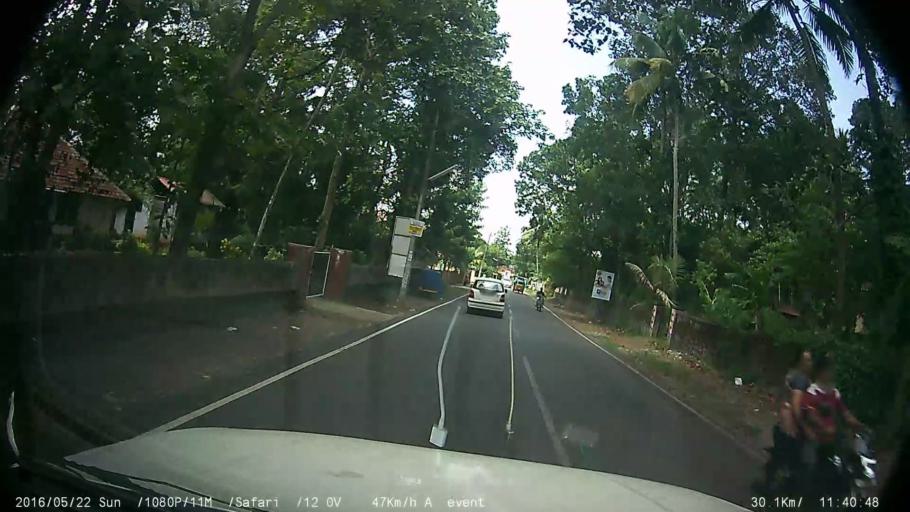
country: IN
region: Kerala
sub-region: Kottayam
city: Kottayam
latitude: 9.5527
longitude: 76.5183
